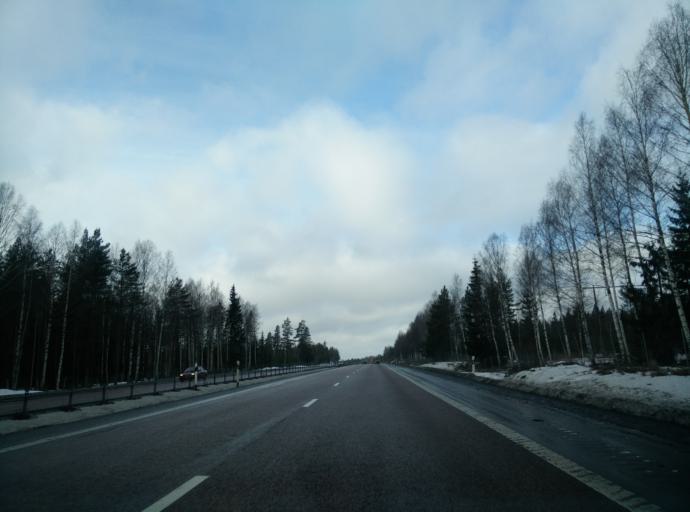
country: SE
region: Gaevleborg
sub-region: Gavle Kommun
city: Valbo
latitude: 60.6281
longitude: 16.9368
